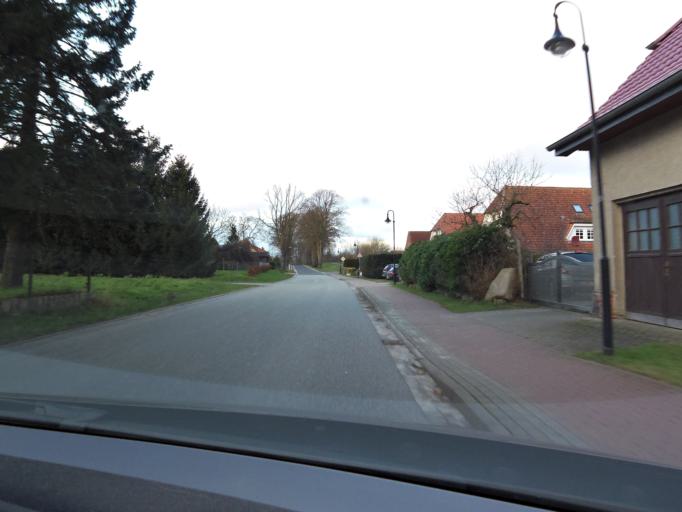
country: DE
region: Mecklenburg-Vorpommern
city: Zarrentin
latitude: 53.5575
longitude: 10.9089
